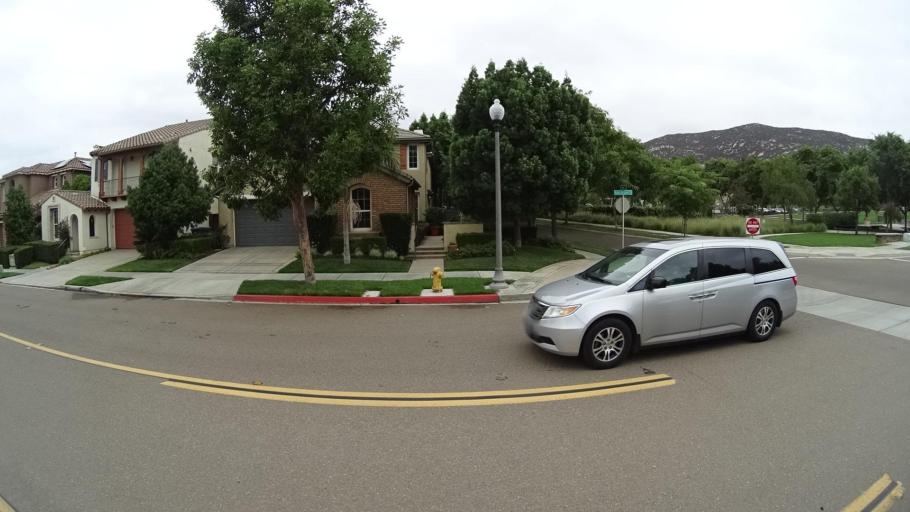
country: US
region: California
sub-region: San Diego County
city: Fairbanks Ranch
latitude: 33.0259
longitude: -117.1106
